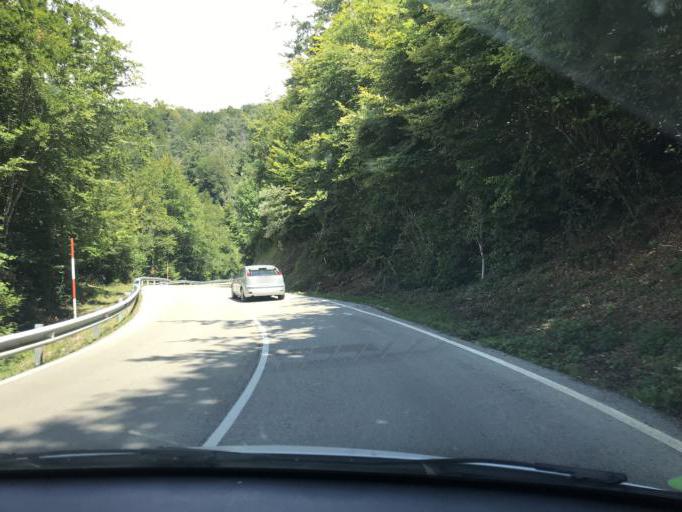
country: ES
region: Cantabria
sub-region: Provincia de Cantabria
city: Cabezon de Liebana
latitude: 43.0716
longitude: -4.4741
